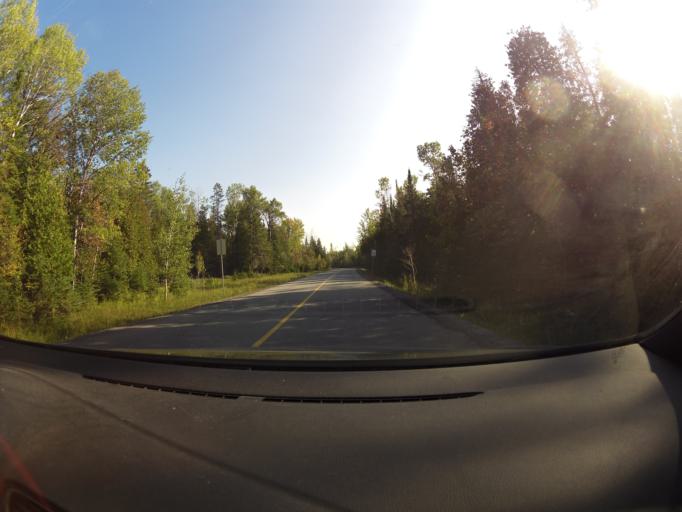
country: CA
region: Ontario
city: Arnprior
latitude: 45.4467
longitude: -76.2780
